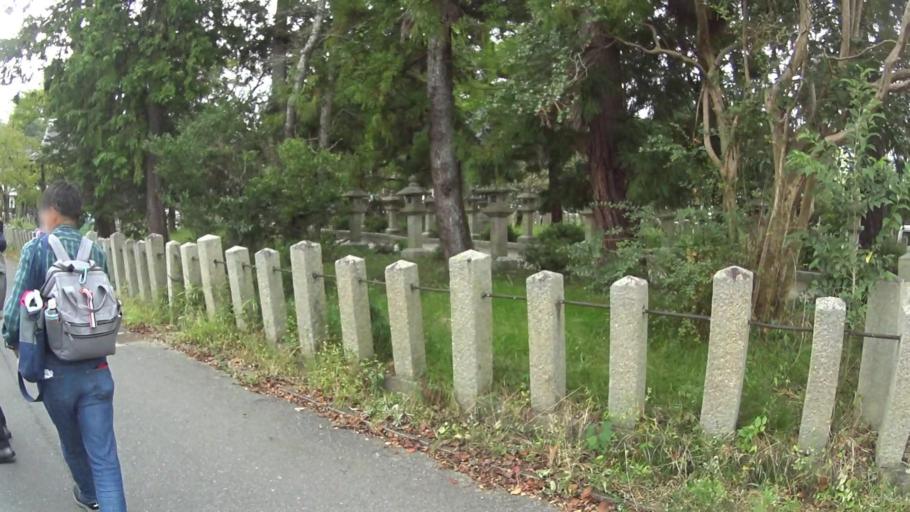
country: JP
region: Shiga Prefecture
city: Nagahama
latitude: 35.3958
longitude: 136.2348
